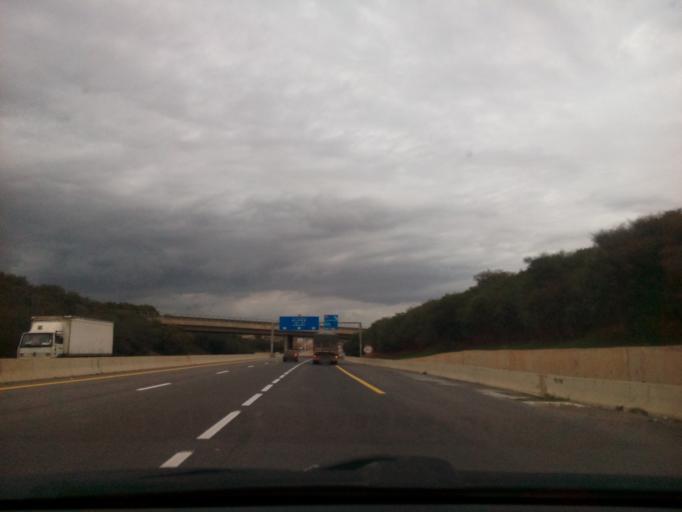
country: DZ
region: Mascara
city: Sig
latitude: 35.5408
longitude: -0.3440
